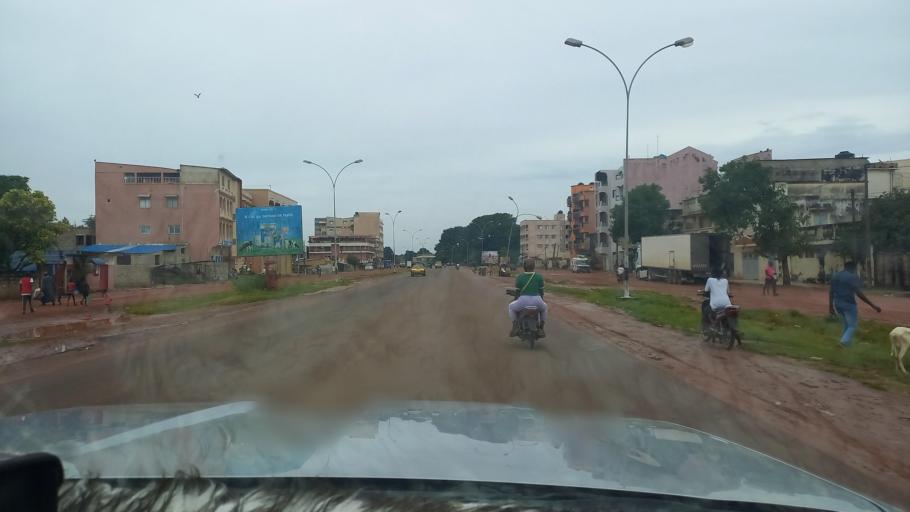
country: SN
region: Ziguinchor
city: Ziguinchor
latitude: 12.5577
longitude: -16.2663
